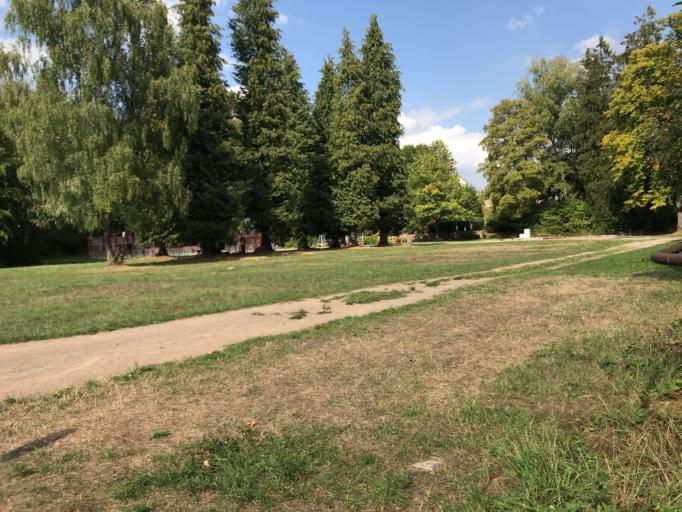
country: FR
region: Lorraine
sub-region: Departement de Meurthe-et-Moselle
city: Thil
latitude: 49.4955
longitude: 5.9130
